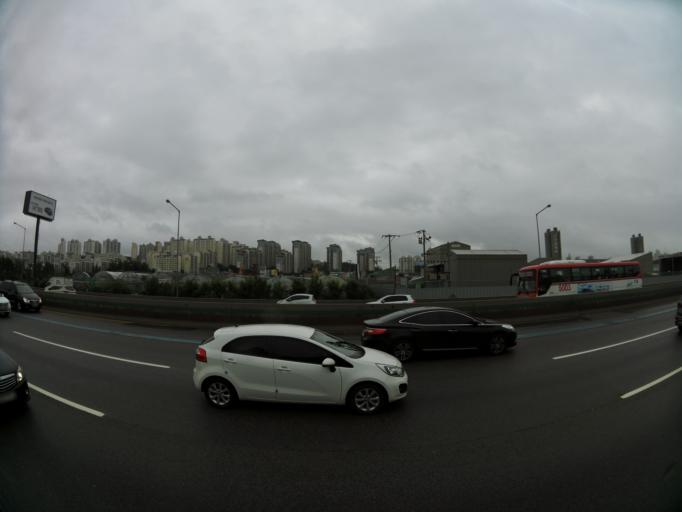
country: KR
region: Gyeonggi-do
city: Suwon-si
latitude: 37.2985
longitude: 127.1035
